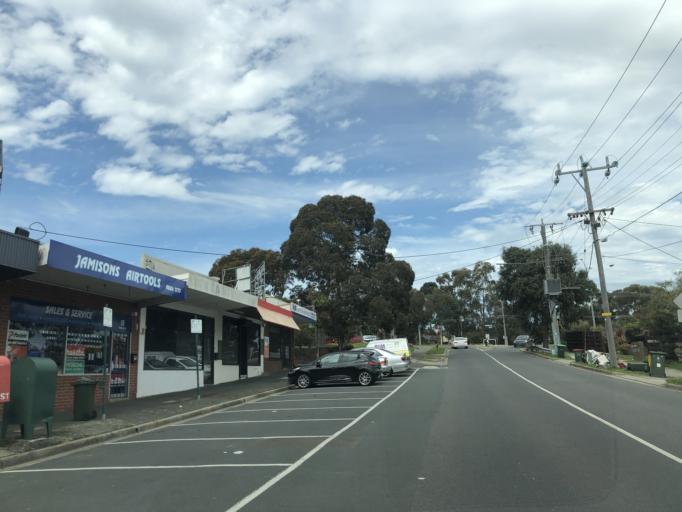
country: AU
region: Victoria
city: Burwood East
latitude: -37.8505
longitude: 145.1425
